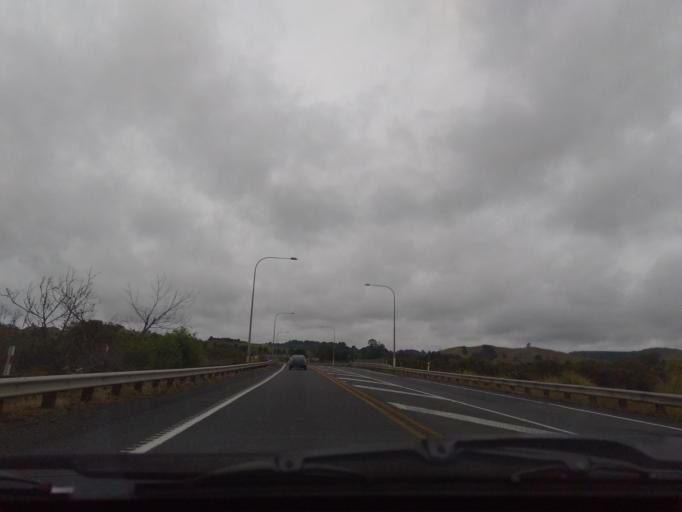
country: NZ
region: Northland
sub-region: Whangarei
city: Whangarei
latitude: -35.8368
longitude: 174.3223
